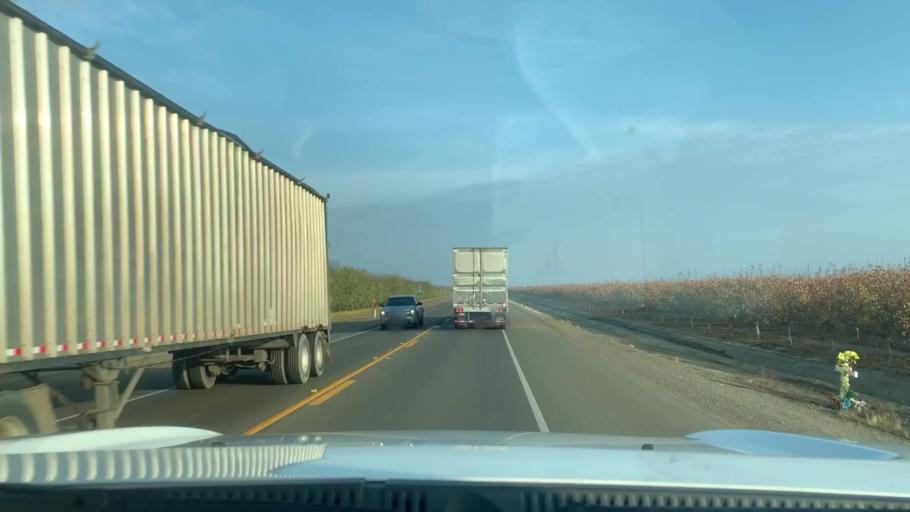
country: US
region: California
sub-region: Kings County
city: Kettleman City
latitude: 36.0142
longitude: -119.9592
